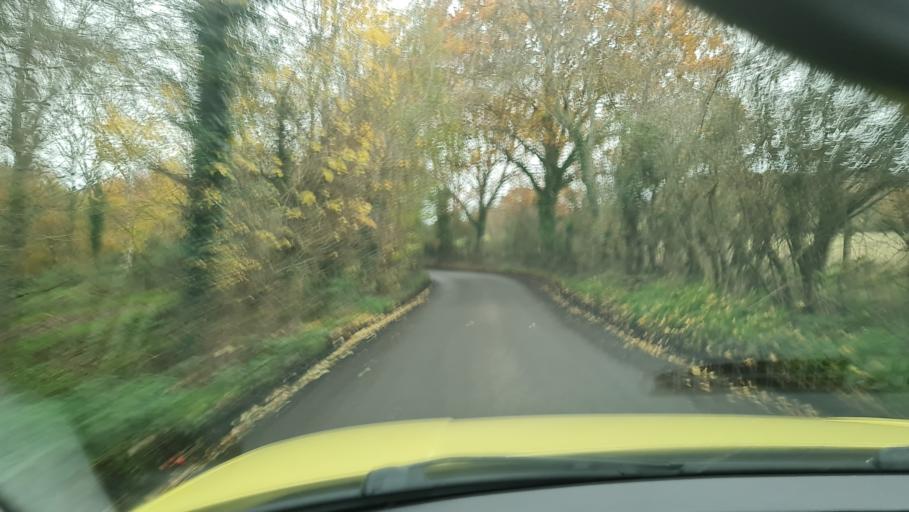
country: GB
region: England
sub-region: Hampshire
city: Yateley
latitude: 51.3548
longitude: -0.8253
